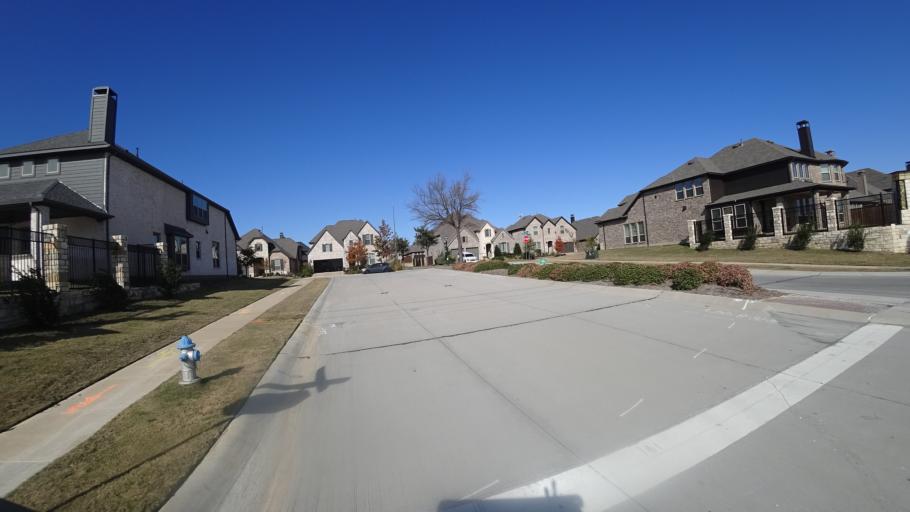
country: US
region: Texas
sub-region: Denton County
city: The Colony
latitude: 33.0240
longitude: -96.8969
